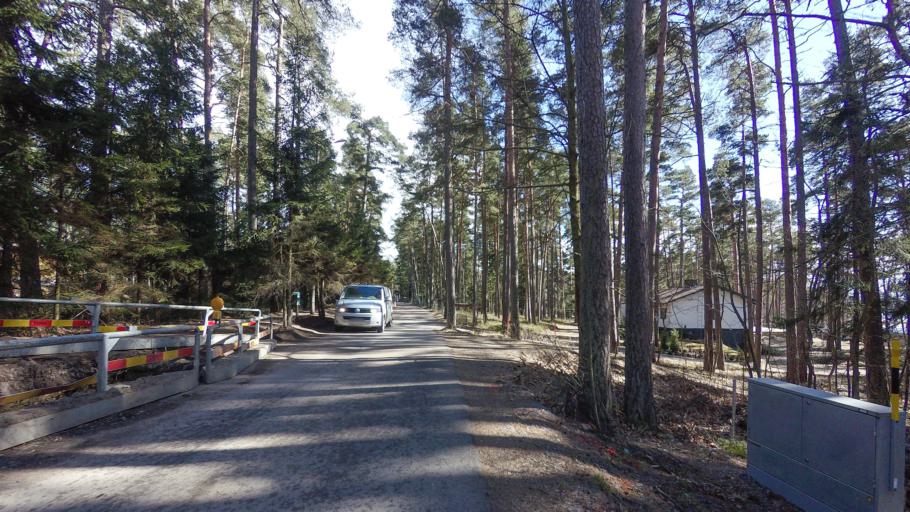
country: FI
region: Uusimaa
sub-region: Helsinki
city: Vantaa
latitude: 60.1927
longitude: 25.1358
